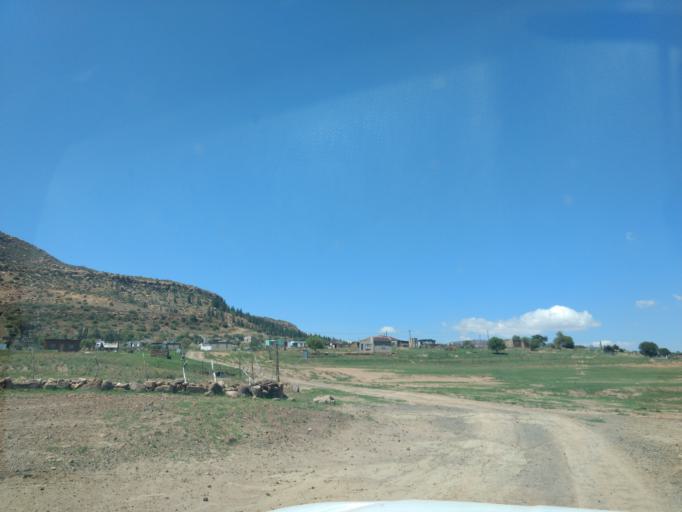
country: LS
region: Maseru
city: Maseru
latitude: -29.4019
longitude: 27.4342
